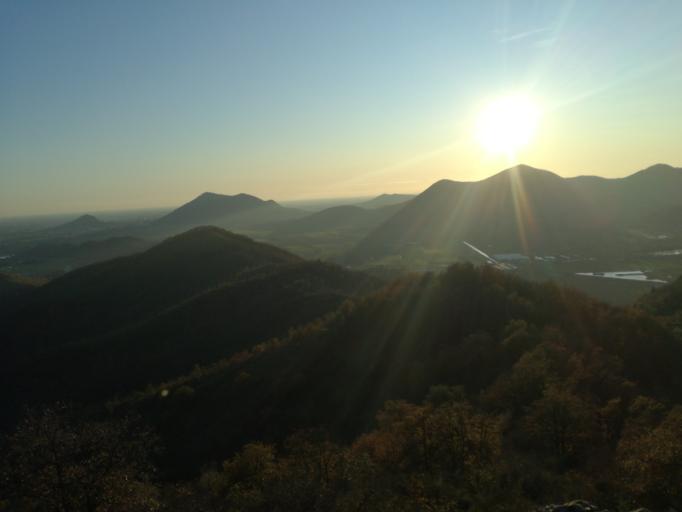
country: IT
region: Veneto
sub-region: Provincia di Padova
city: Montegrotto Terme
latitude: 45.3102
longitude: 11.7726
